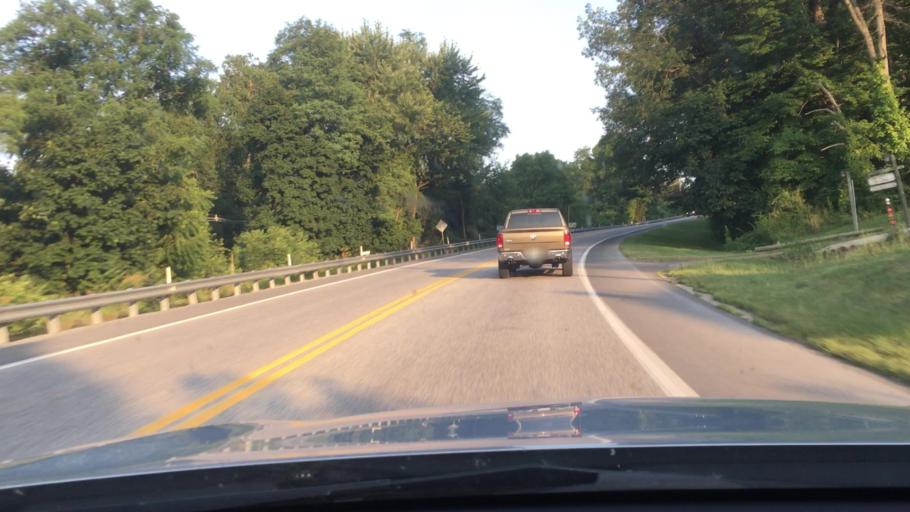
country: US
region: Pennsylvania
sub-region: York County
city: Dover
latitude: 40.0770
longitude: -76.9269
